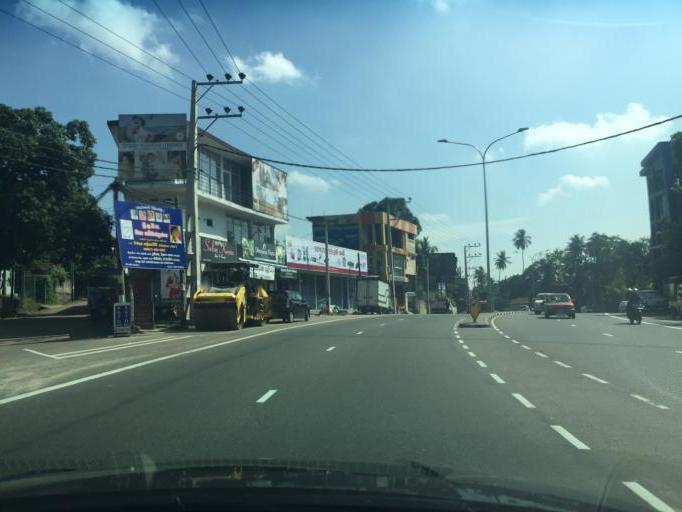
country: LK
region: Western
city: Maharagama
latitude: 6.8173
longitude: 79.9185
